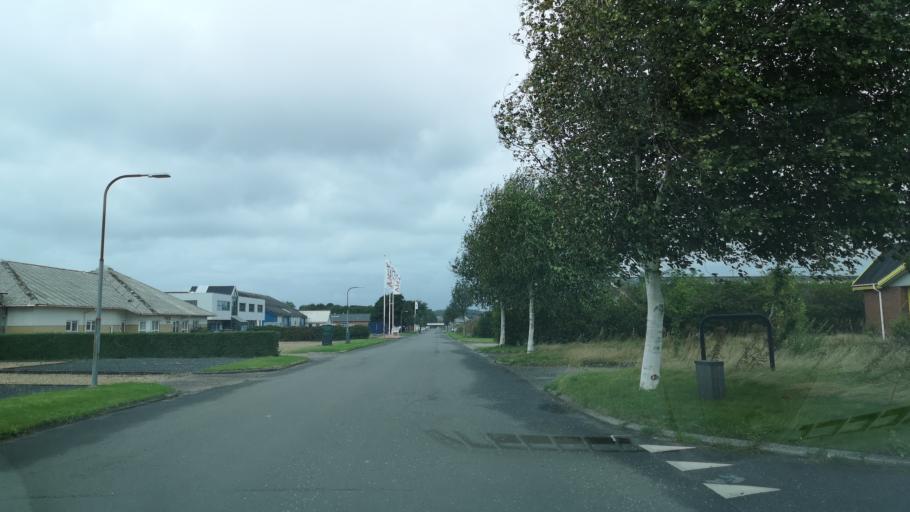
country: DK
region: Central Jutland
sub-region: Ringkobing-Skjern Kommune
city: Videbaek
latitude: 56.0895
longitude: 8.6462
